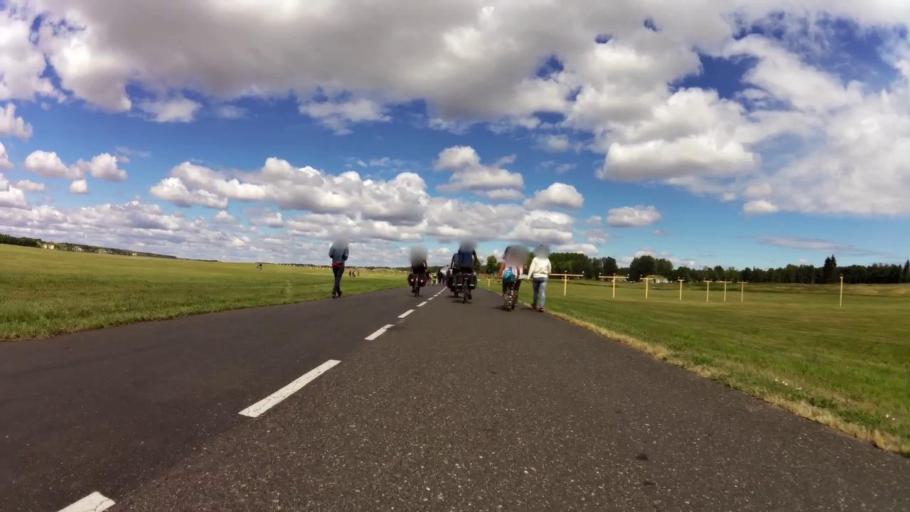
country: PL
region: West Pomeranian Voivodeship
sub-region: Powiat swidwinski
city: Swidwin
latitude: 53.7836
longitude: 15.8554
